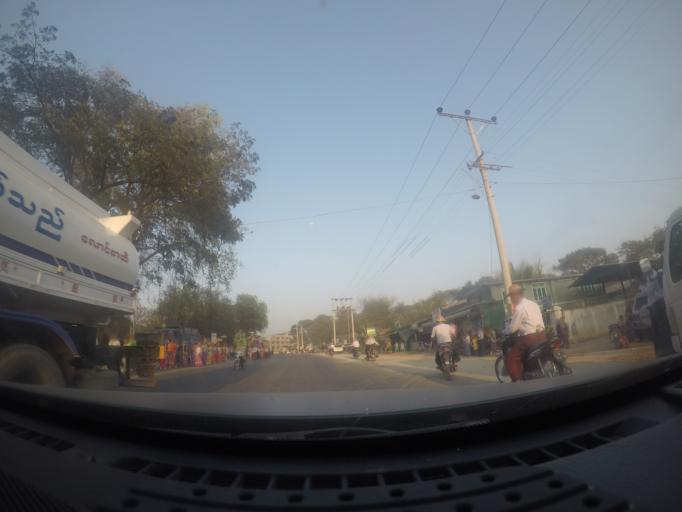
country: MM
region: Mandalay
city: Yamethin
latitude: 20.7557
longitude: 96.3109
